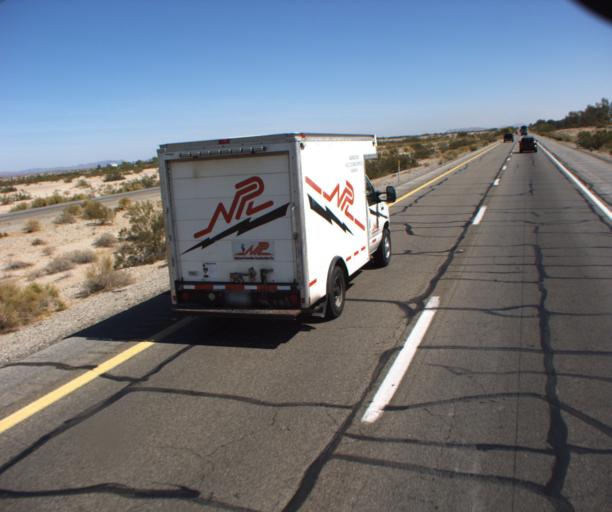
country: US
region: Arizona
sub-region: Yuma County
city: Wellton
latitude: 32.6519
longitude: -114.1839
